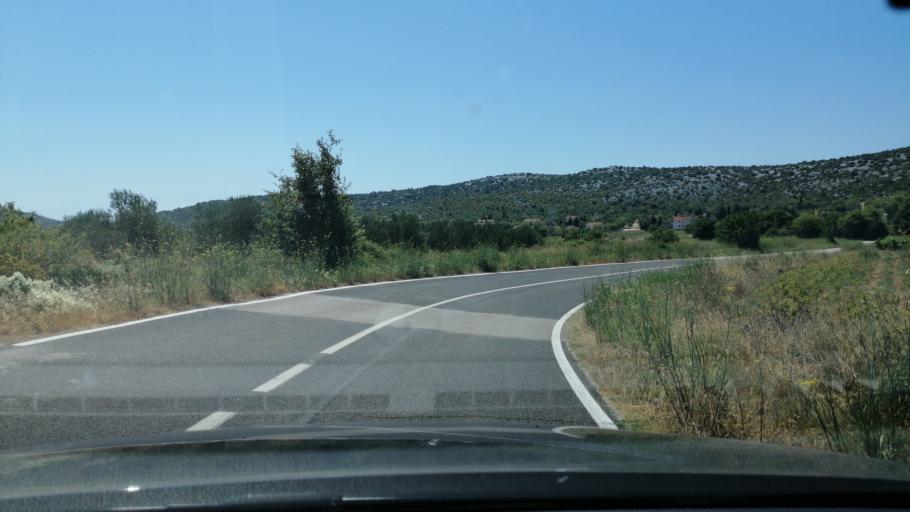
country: HR
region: Sibensko-Kniniska
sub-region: Grad Sibenik
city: Pirovac
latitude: 43.8762
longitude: 15.6817
